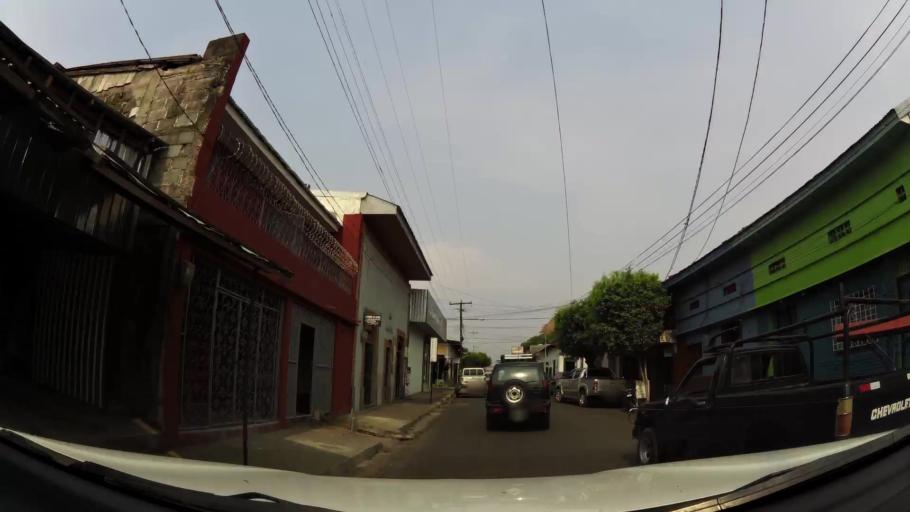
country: NI
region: Chinandega
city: Chinandega
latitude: 12.6286
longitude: -87.1307
